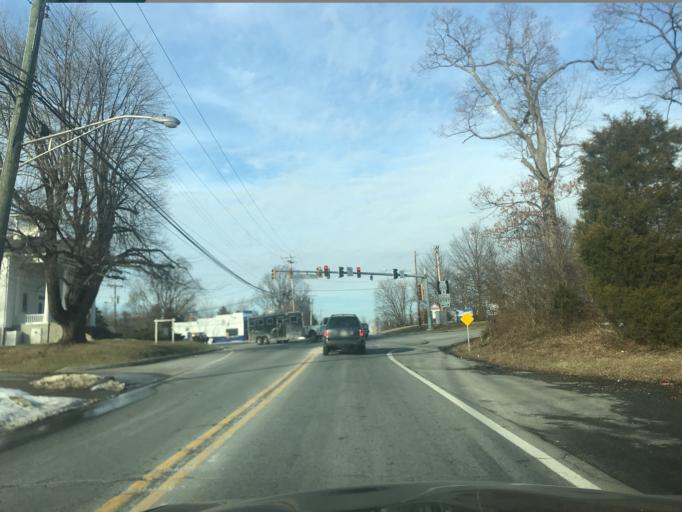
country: US
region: Maryland
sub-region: Montgomery County
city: Olney
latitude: 39.2210
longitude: -77.0600
